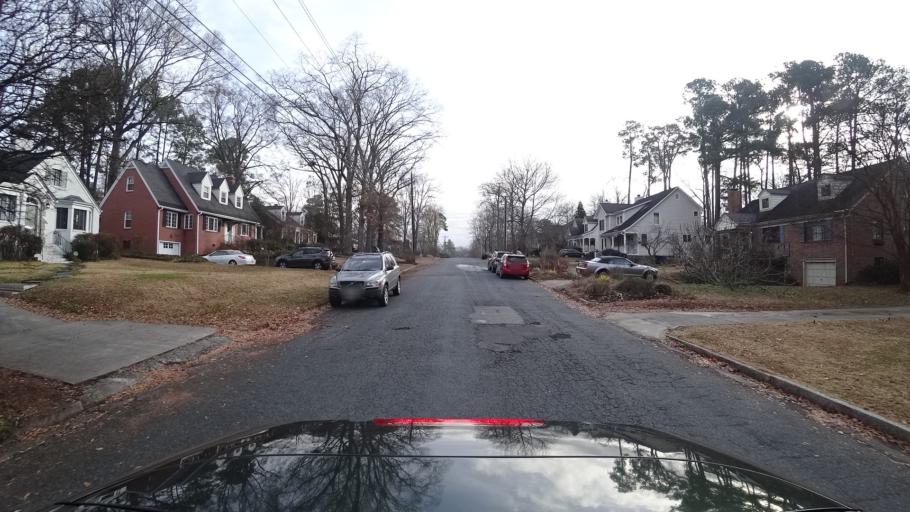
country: US
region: North Carolina
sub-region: Durham County
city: Durham
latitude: 36.0128
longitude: -78.8982
